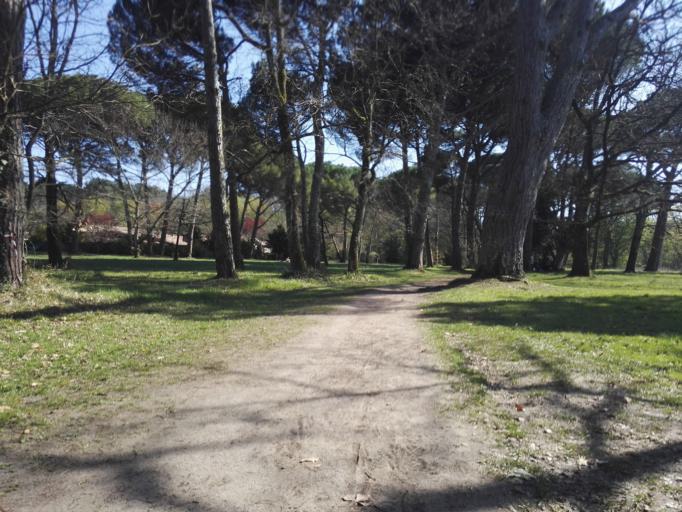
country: FR
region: Aquitaine
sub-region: Departement de la Gironde
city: Gradignan
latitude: 44.7680
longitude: -0.6055
